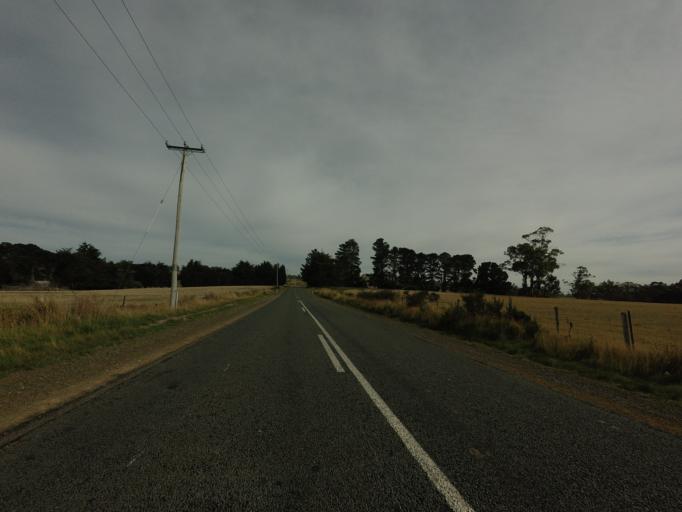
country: AU
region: Tasmania
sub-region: Brighton
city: Bridgewater
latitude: -42.3932
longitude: 147.4322
